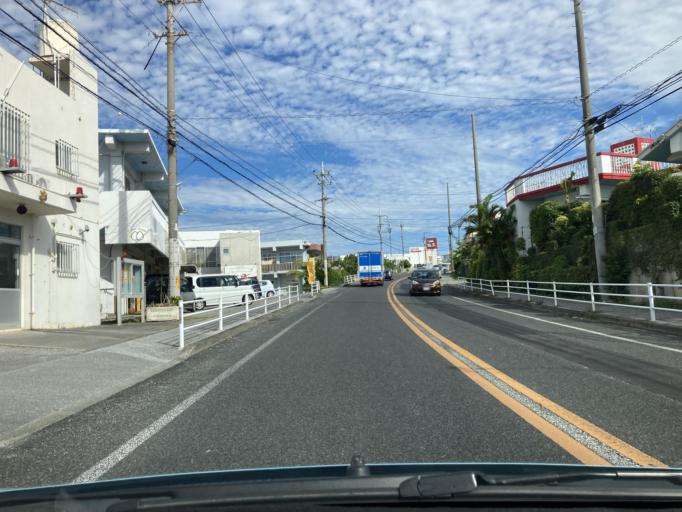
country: JP
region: Okinawa
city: Ishikawa
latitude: 26.4020
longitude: 127.7244
